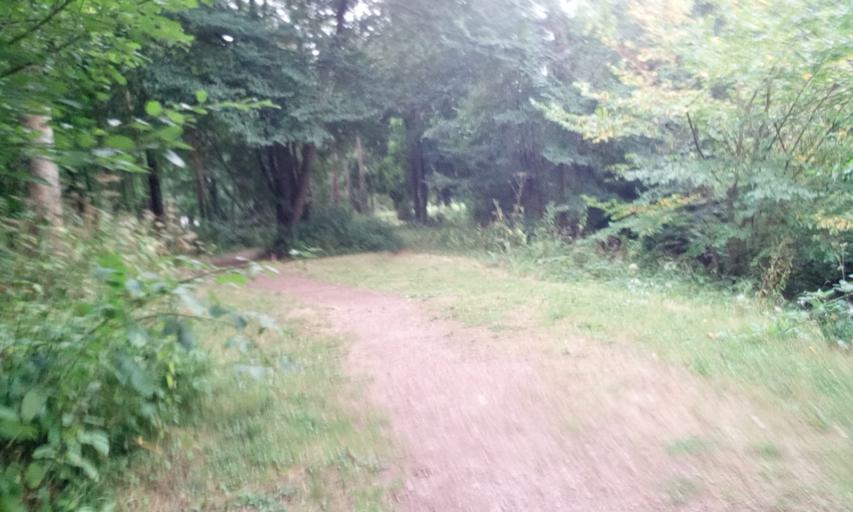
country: FR
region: Lower Normandy
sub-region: Departement du Calvados
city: Verson
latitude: 49.1517
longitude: -0.4502
